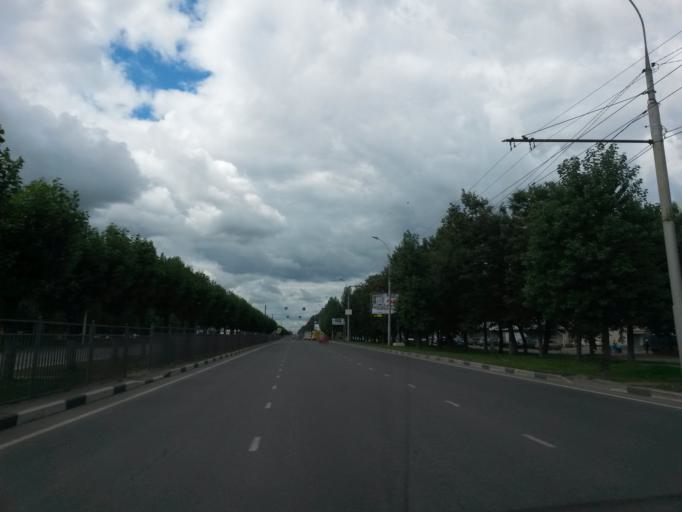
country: RU
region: Jaroslavl
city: Yaroslavl
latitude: 57.6794
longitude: 39.7961
